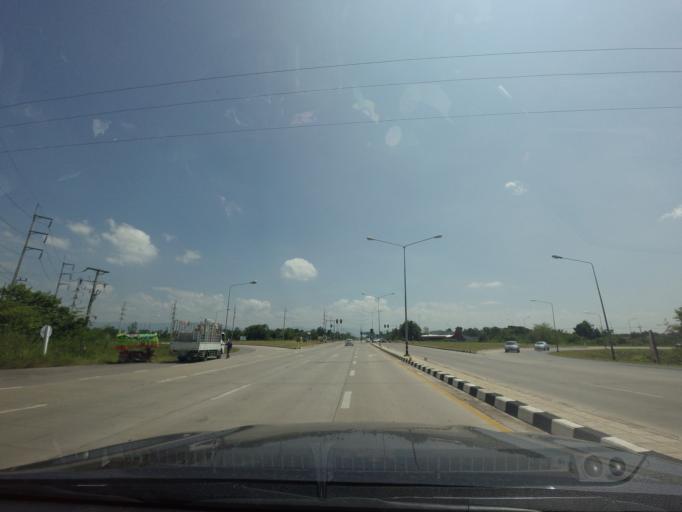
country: TH
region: Phetchabun
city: Lom Sak
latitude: 16.7657
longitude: 101.1848
